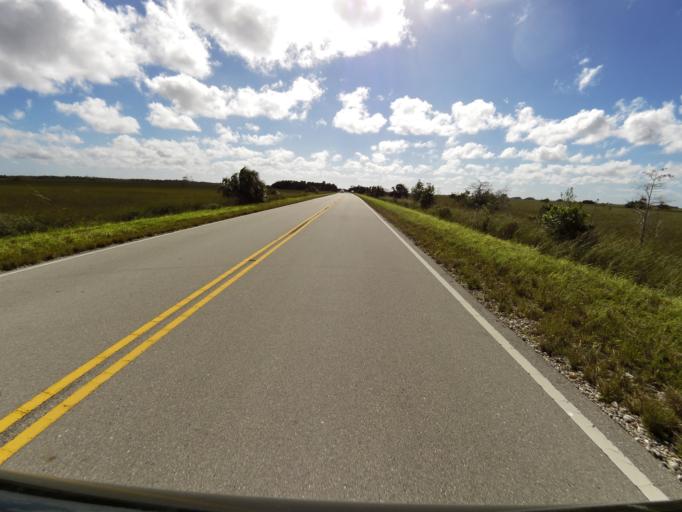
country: US
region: Florida
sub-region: Miami-Dade County
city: Florida City
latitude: 25.3664
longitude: -80.8188
